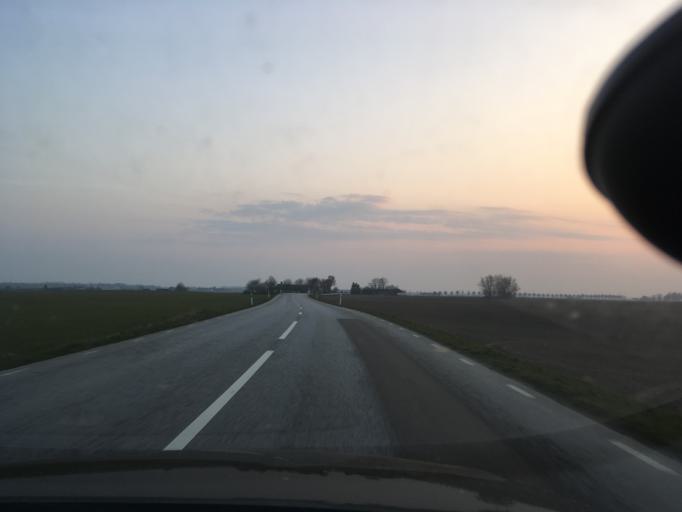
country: SE
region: Skane
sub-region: Ystads Kommun
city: Kopingebro
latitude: 55.4629
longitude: 14.0349
